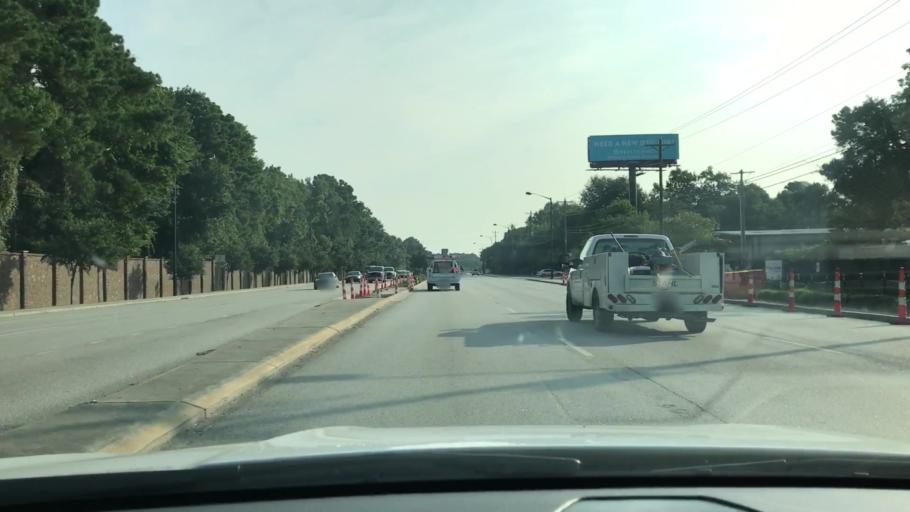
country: US
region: South Carolina
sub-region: Charleston County
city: Isle of Palms
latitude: 32.8418
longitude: -79.8158
